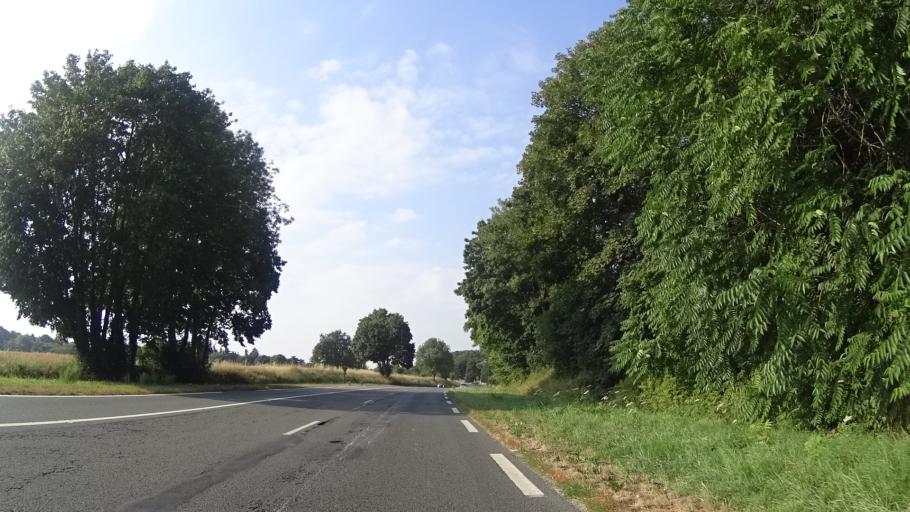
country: FR
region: Ile-de-France
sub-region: Departement du Val-d'Oise
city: Luzarches
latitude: 49.1140
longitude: 2.4305
